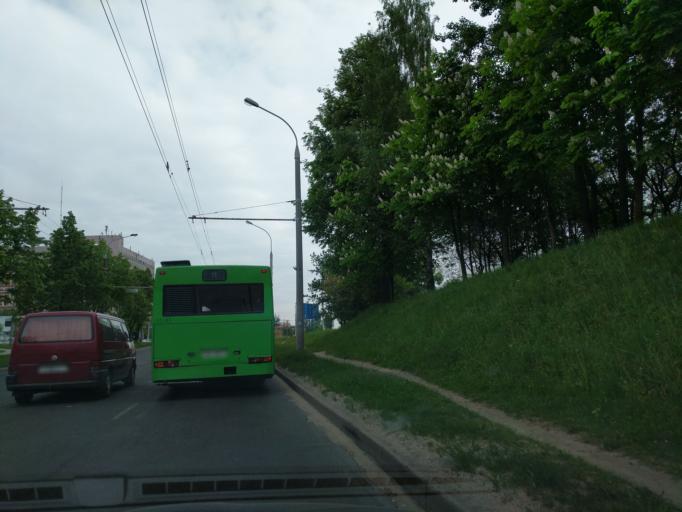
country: BY
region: Minsk
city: Novoye Medvezhino
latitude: 53.9058
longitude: 27.4627
